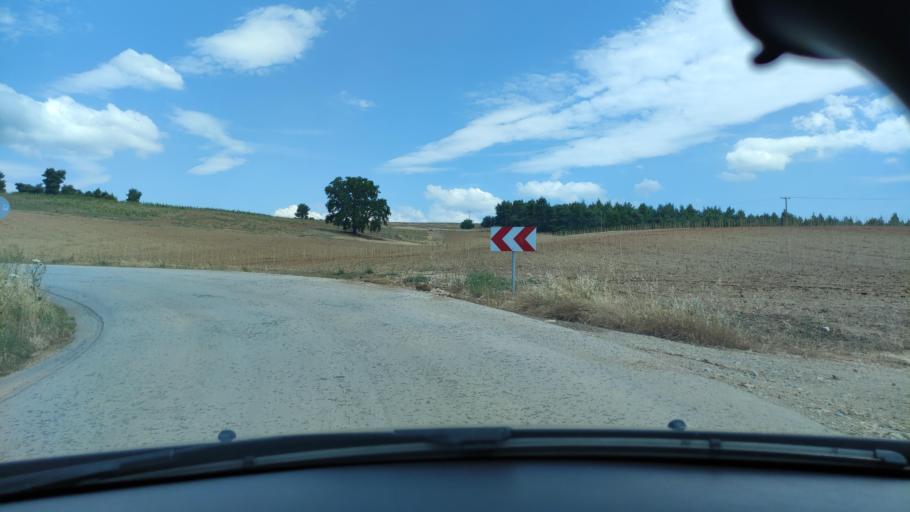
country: GR
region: Central Greece
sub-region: Nomos Evvoias
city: Afration
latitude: 38.5202
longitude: 23.7501
